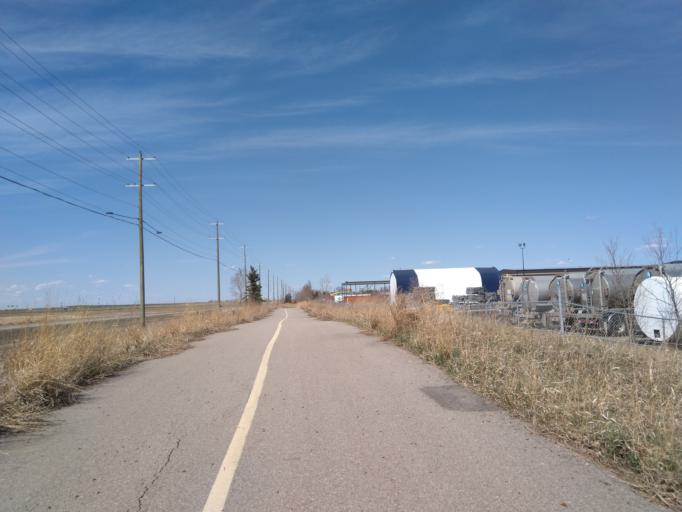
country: CA
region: Alberta
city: Chestermere
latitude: 50.9660
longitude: -113.9115
